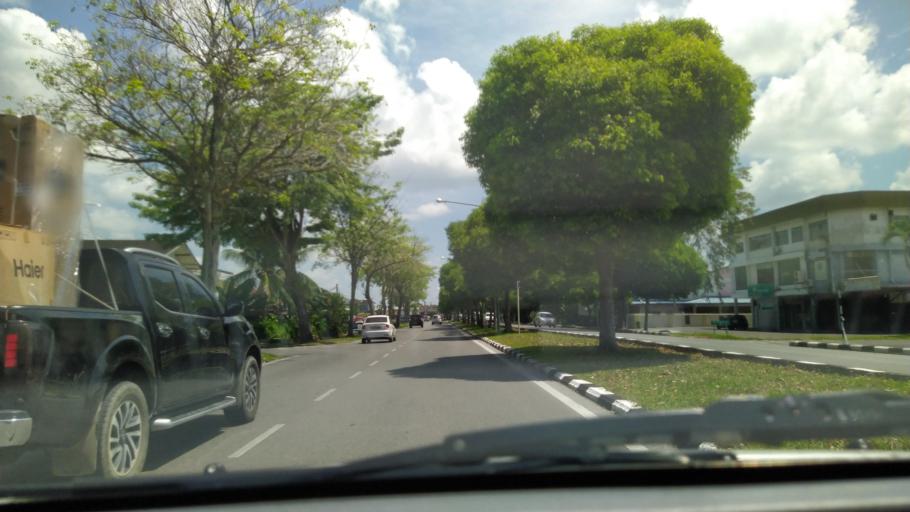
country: MY
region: Sarawak
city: Sibu
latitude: 2.3047
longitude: 111.8309
